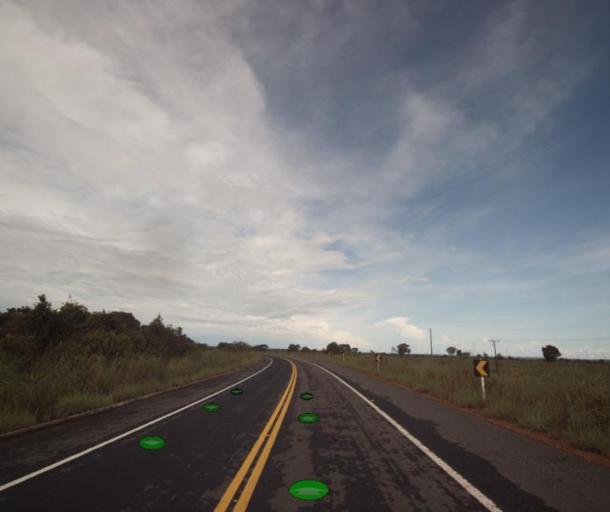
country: BR
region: Goias
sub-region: Sao Miguel Do Araguaia
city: Sao Miguel do Araguaia
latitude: -13.2845
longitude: -50.4904
